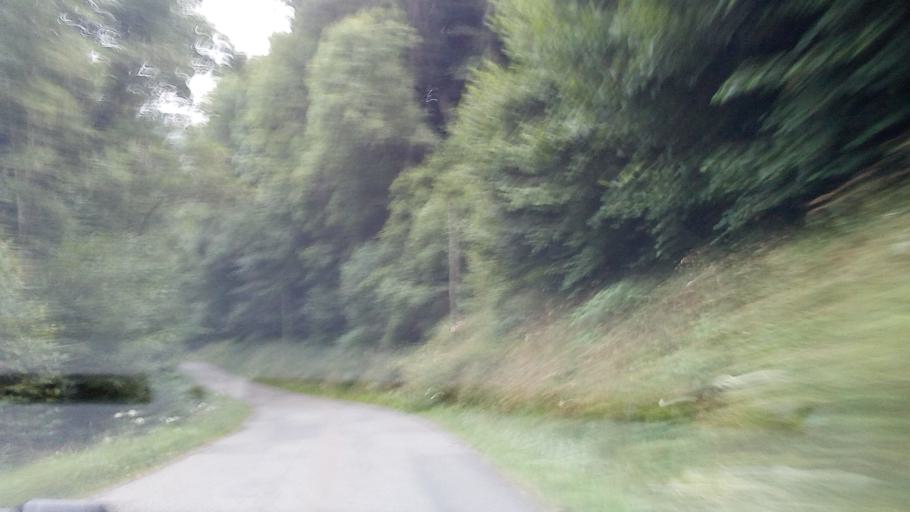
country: FR
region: Midi-Pyrenees
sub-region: Departement des Hautes-Pyrenees
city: Cauterets
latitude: 42.9445
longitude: -0.1821
